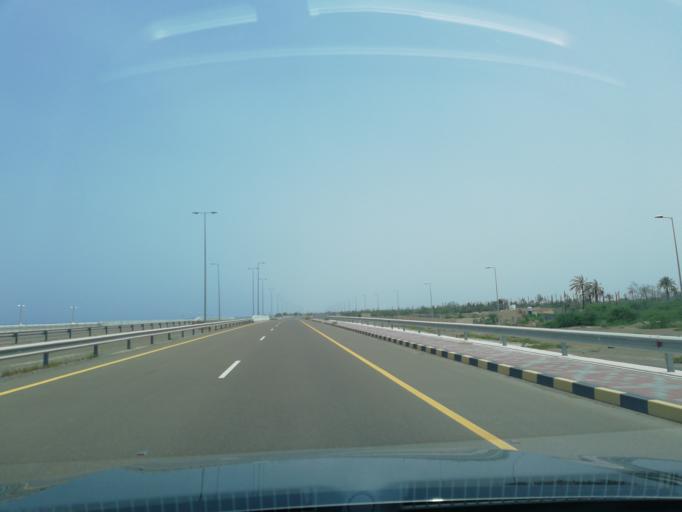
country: OM
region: Al Batinah
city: Al Liwa'
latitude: 24.6300
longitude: 56.5279
